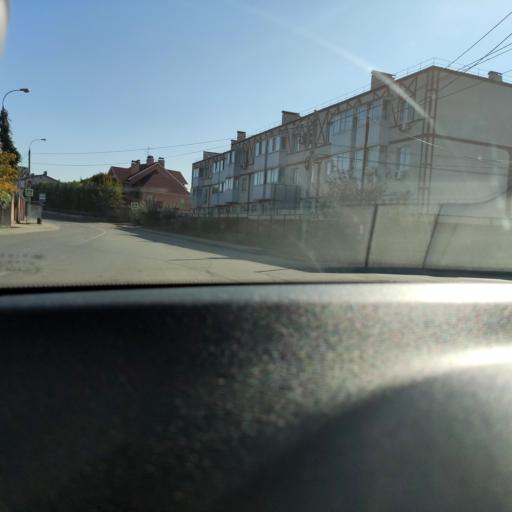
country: RU
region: Samara
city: Samara
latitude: 53.2686
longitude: 50.1981
